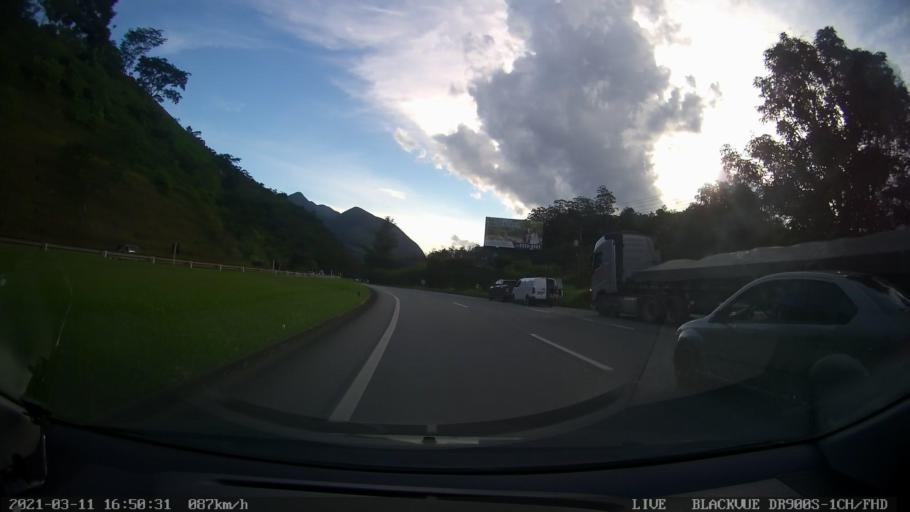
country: BR
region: Rio de Janeiro
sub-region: Petropolis
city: Petropolis
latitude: -22.4278
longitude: -43.1648
